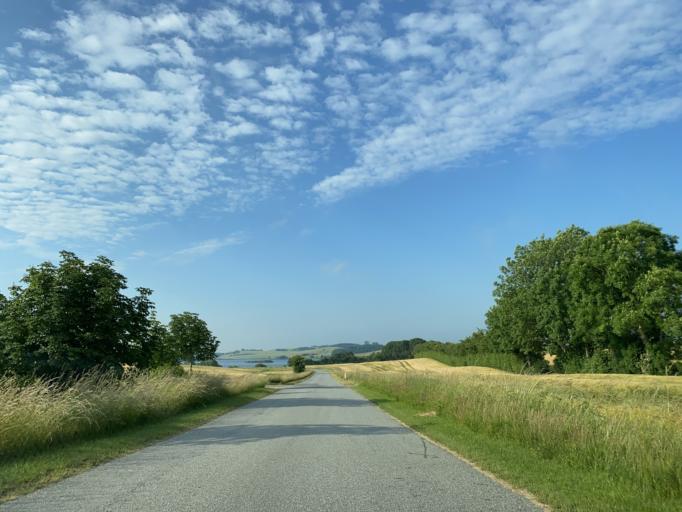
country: DK
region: South Denmark
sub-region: Haderslev Kommune
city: Haderslev
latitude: 55.1776
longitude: 9.4814
